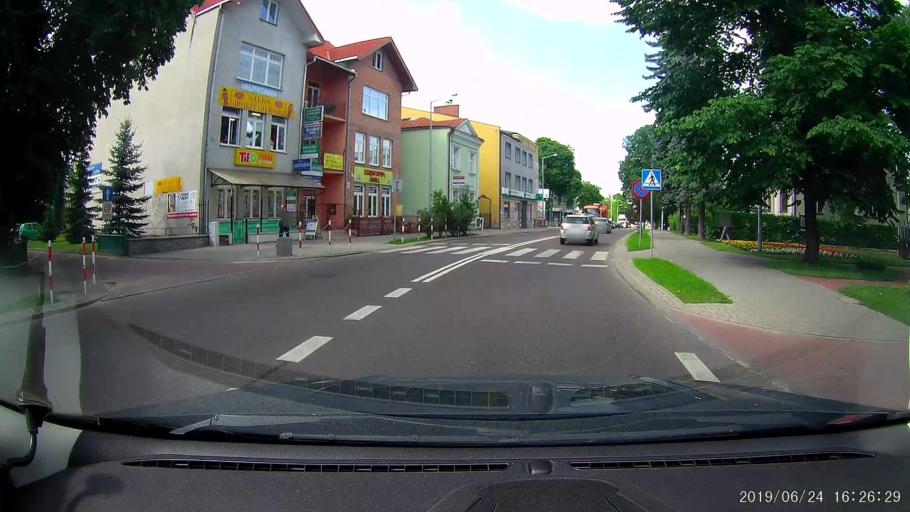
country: PL
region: Lublin Voivodeship
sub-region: Powiat tomaszowski
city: Tomaszow Lubelski
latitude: 50.4474
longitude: 23.4162
